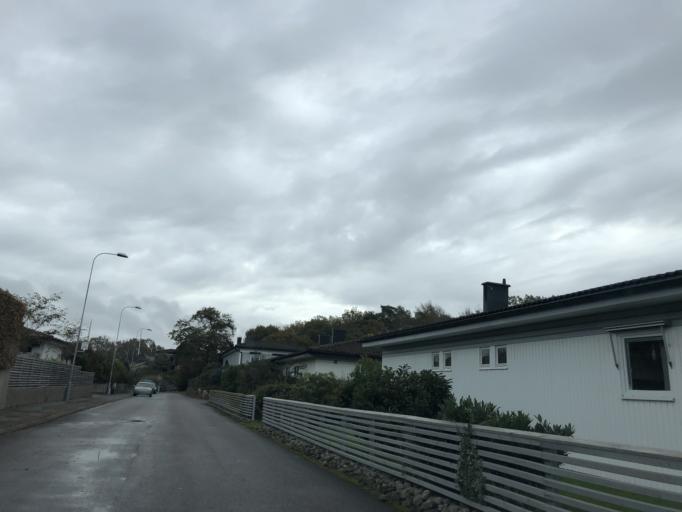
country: SE
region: Vaestra Goetaland
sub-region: Goteborg
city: Majorna
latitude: 57.6632
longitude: 11.8659
